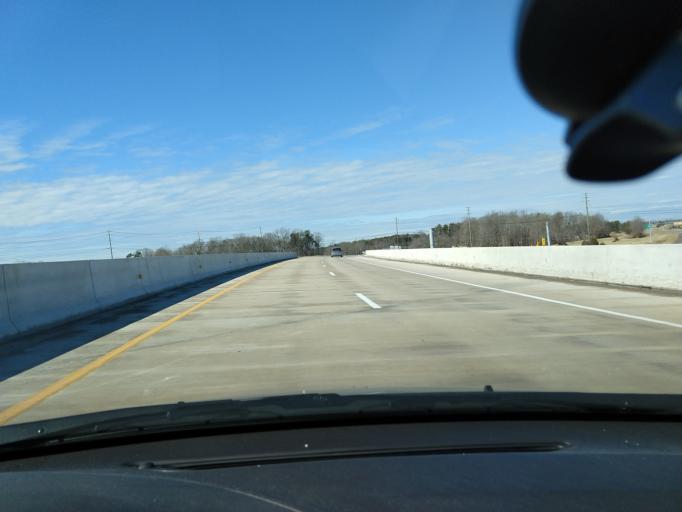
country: US
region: North Carolina
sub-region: Guilford County
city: Oak Ridge
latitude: 36.1240
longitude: -79.9615
